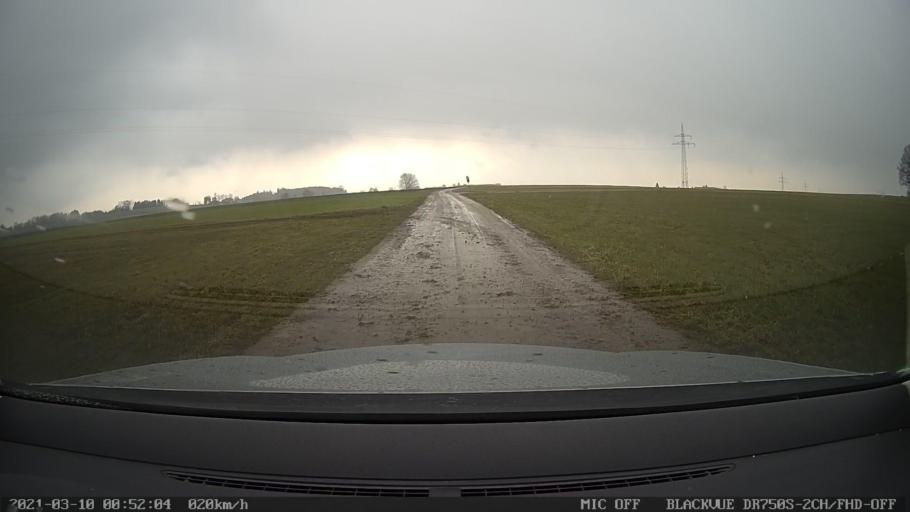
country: DE
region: Bavaria
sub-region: Upper Bavaria
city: Griesstatt
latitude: 47.9934
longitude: 12.1922
